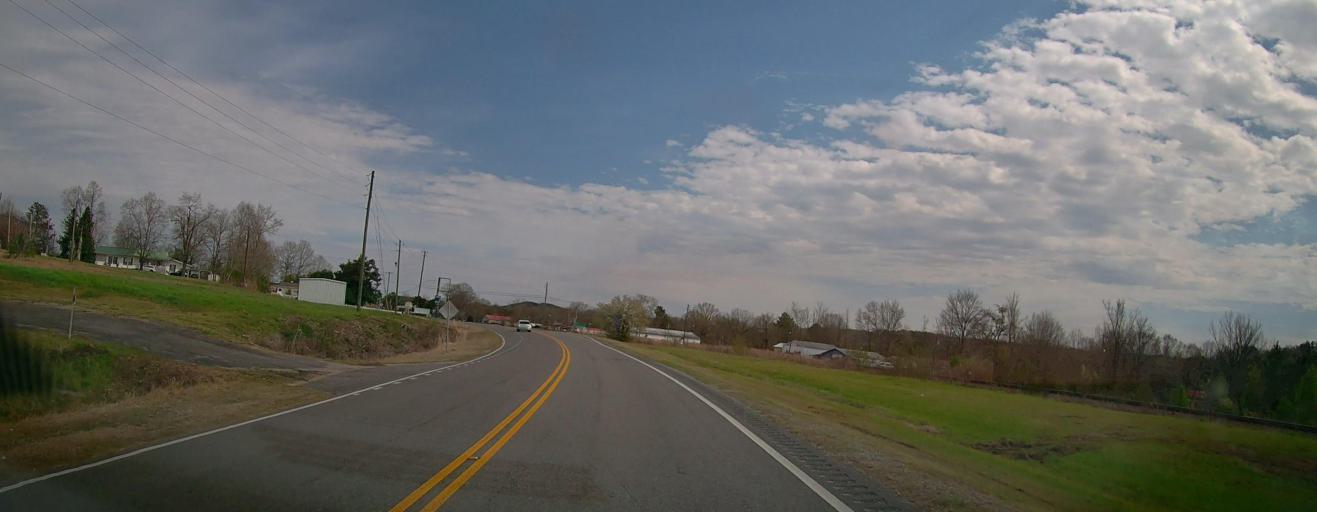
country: US
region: Alabama
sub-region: Walker County
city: Carbon Hill
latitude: 33.8909
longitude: -87.5341
